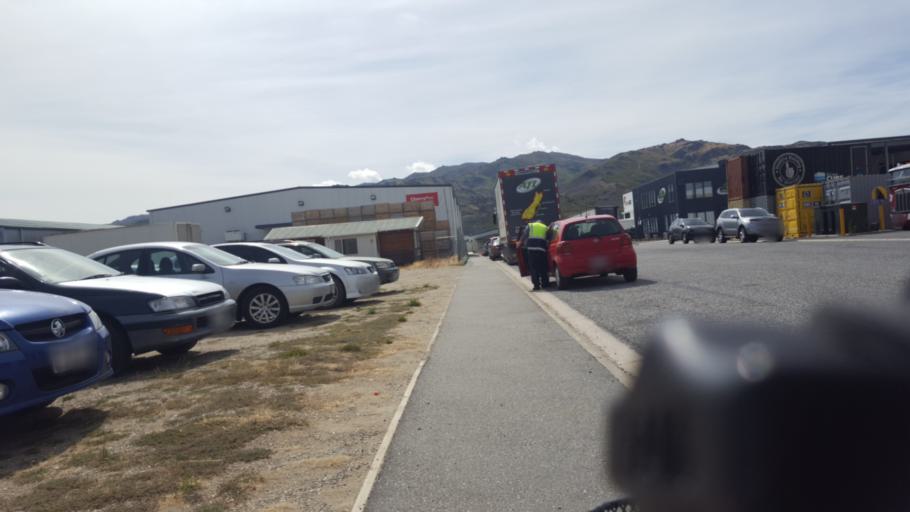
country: NZ
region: Otago
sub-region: Queenstown-Lakes District
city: Wanaka
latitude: -45.0517
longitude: 169.1896
